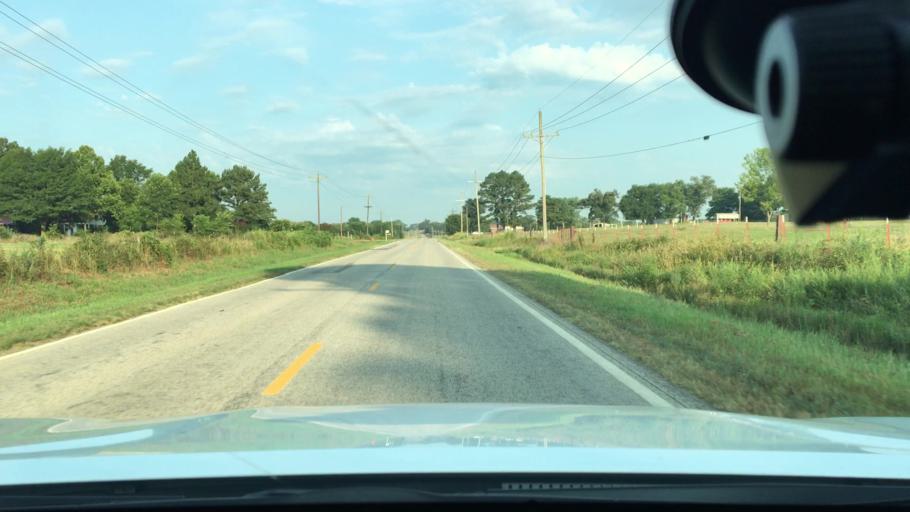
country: US
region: Arkansas
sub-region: Johnson County
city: Coal Hill
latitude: 35.3373
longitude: -93.6194
